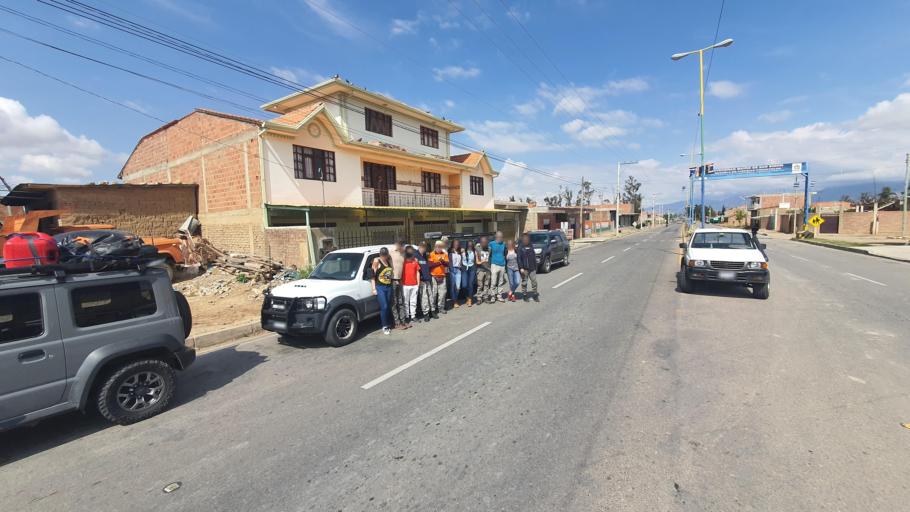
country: BO
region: Cochabamba
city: Arani
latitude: -17.5686
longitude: -65.7760
